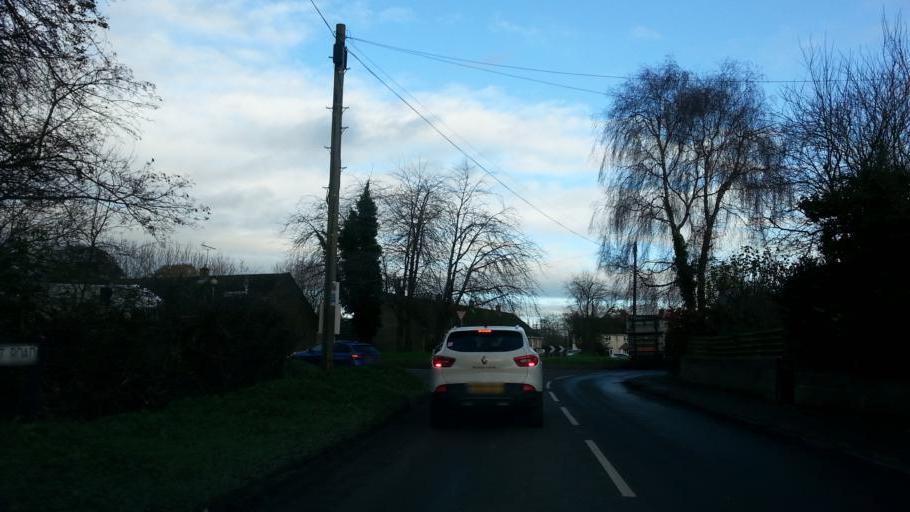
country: GB
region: England
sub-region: Oxfordshire
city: Faringdon
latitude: 51.6256
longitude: -1.5807
